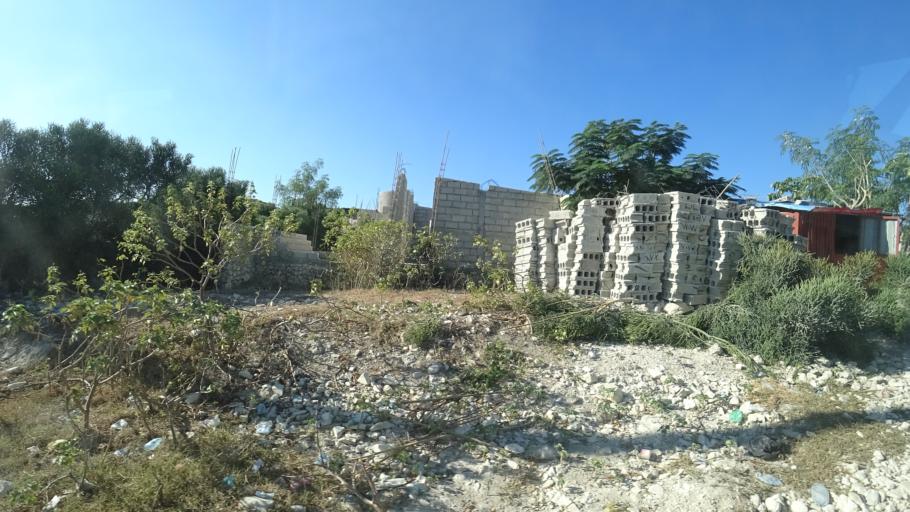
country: HT
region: Ouest
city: Croix des Bouquets
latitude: 18.6724
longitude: -72.2416
